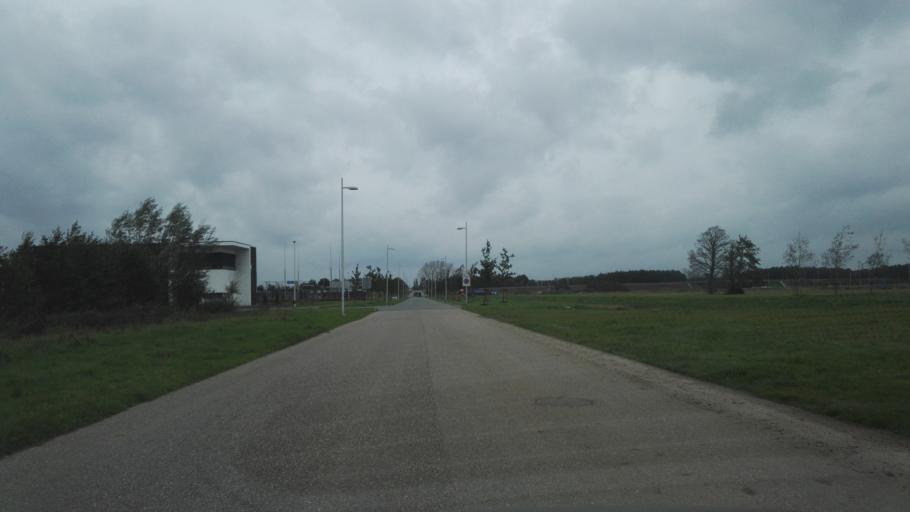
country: NL
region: Gelderland
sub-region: Gemeente Apeldoorn
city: Apeldoorn
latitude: 52.2443
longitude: 6.0051
